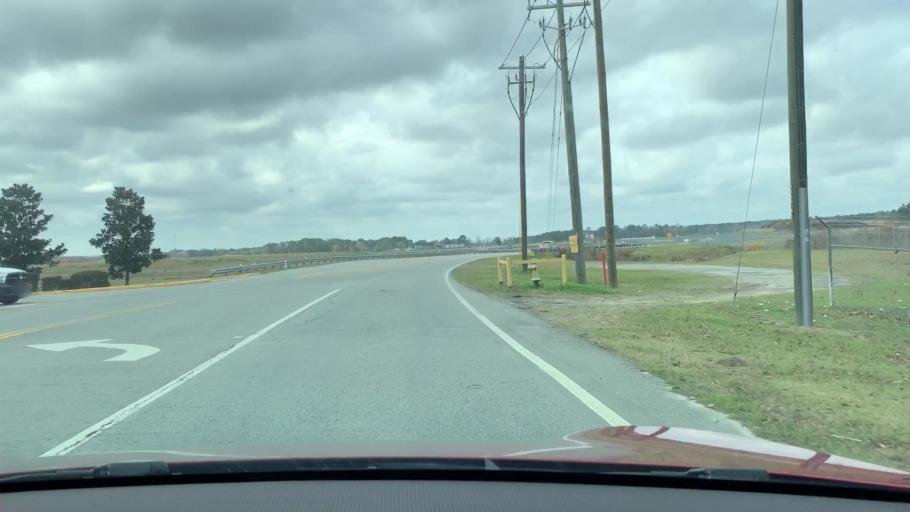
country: US
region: Georgia
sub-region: Chatham County
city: Port Wentworth
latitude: 32.1413
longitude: -81.1978
